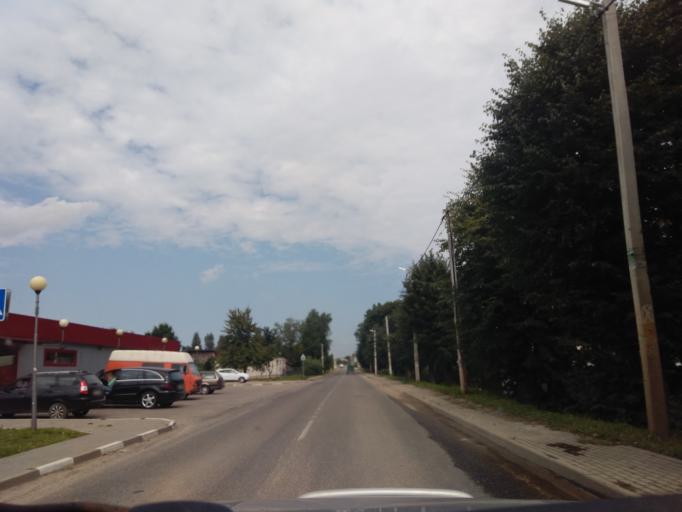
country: BY
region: Minsk
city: Khatsyezhyna
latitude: 53.9111
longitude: 27.3097
